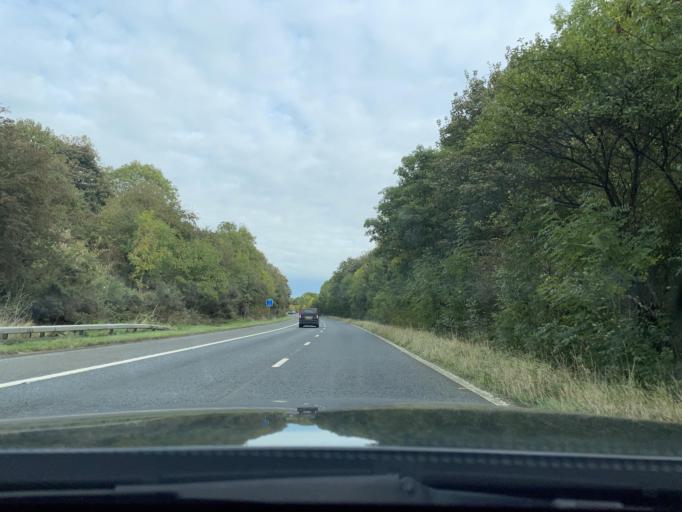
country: GB
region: England
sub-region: Rotherham
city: Bramley
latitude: 53.3958
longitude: -1.2737
